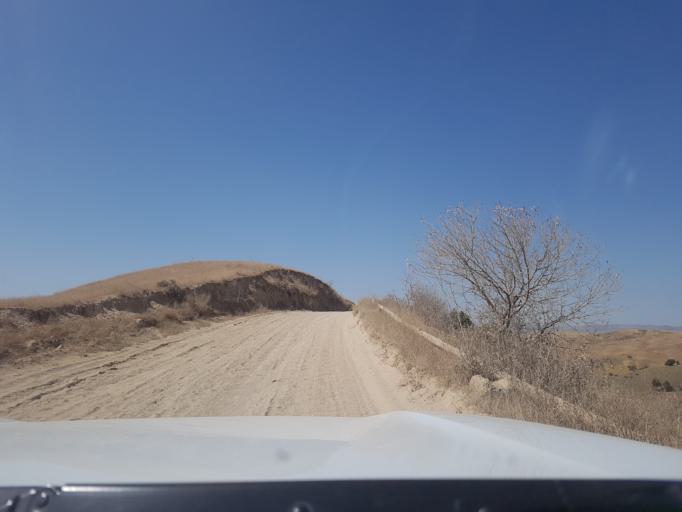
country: TM
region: Ahal
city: Baharly
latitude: 38.2754
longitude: 56.9056
